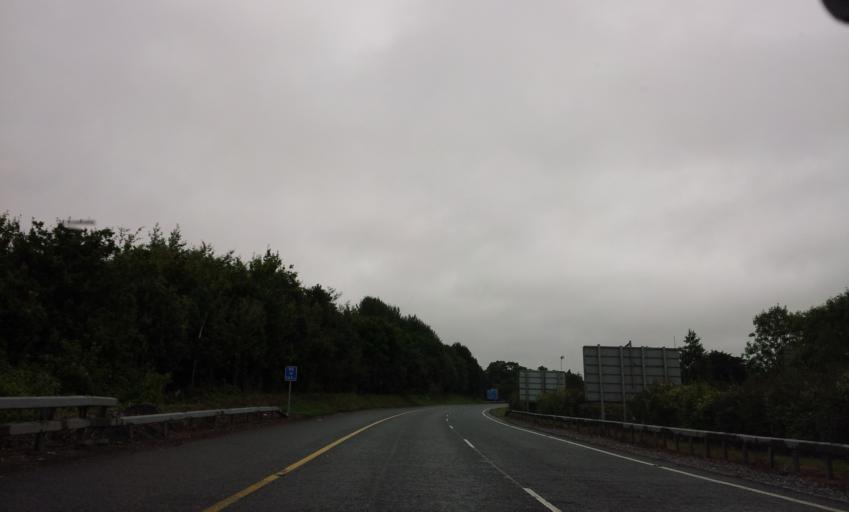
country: IE
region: Munster
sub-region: County Cork
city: Passage West
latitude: 51.9057
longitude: -8.3869
